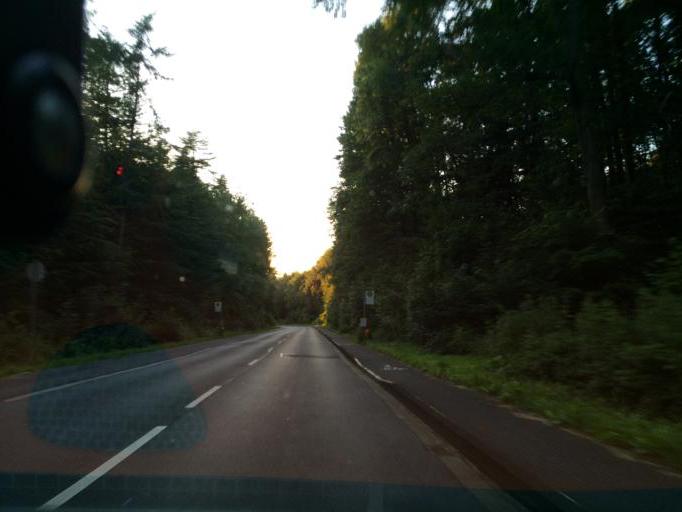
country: DE
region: North Rhine-Westphalia
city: Sankt Augustin
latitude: 50.7357
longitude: 7.1695
